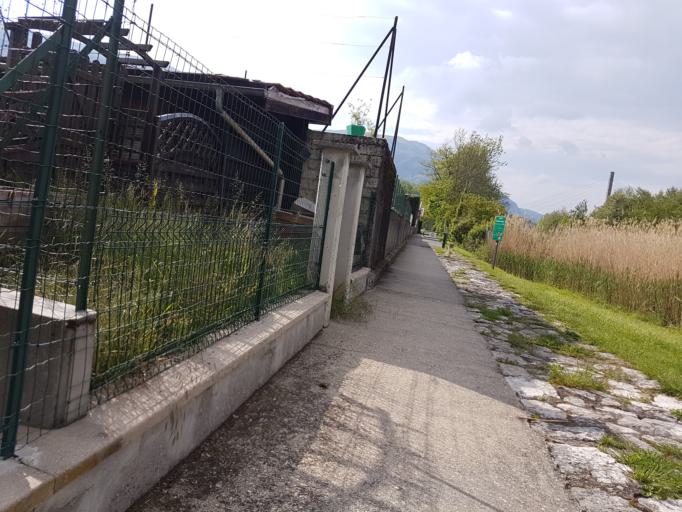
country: FR
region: Rhone-Alpes
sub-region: Departement de la Haute-Savoie
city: Versonnex
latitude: 45.9566
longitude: 5.8341
